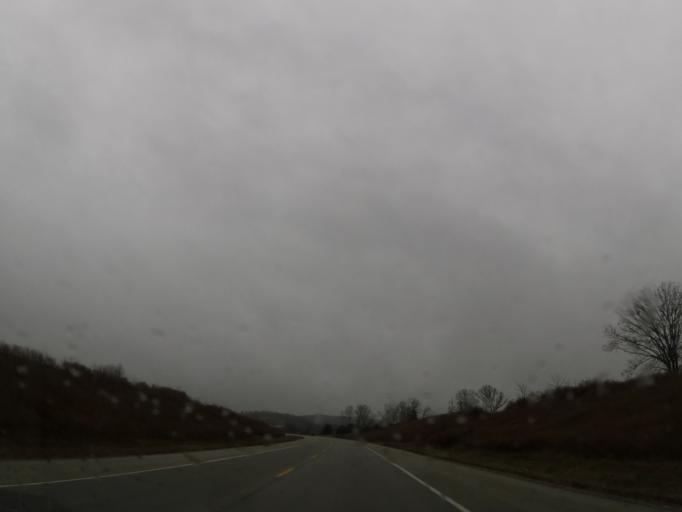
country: US
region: Kentucky
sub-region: Rockcastle County
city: Brodhead
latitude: 37.3584
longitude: -84.4066
